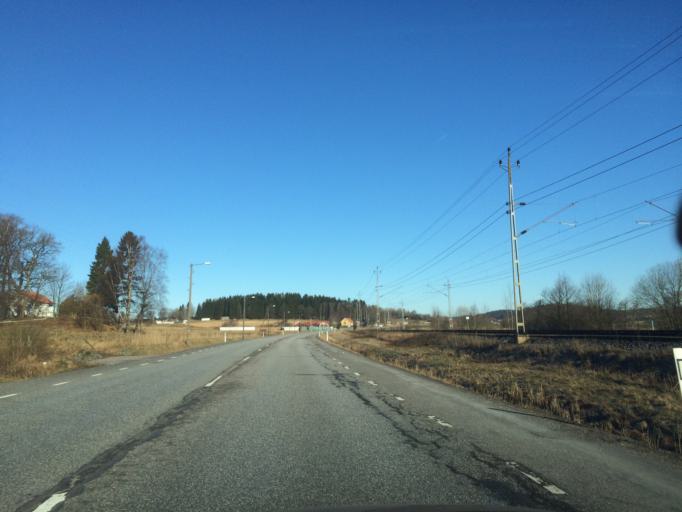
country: SE
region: Vaestra Goetaland
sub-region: Molndal
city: Lindome
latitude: 57.5570
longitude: 12.0868
